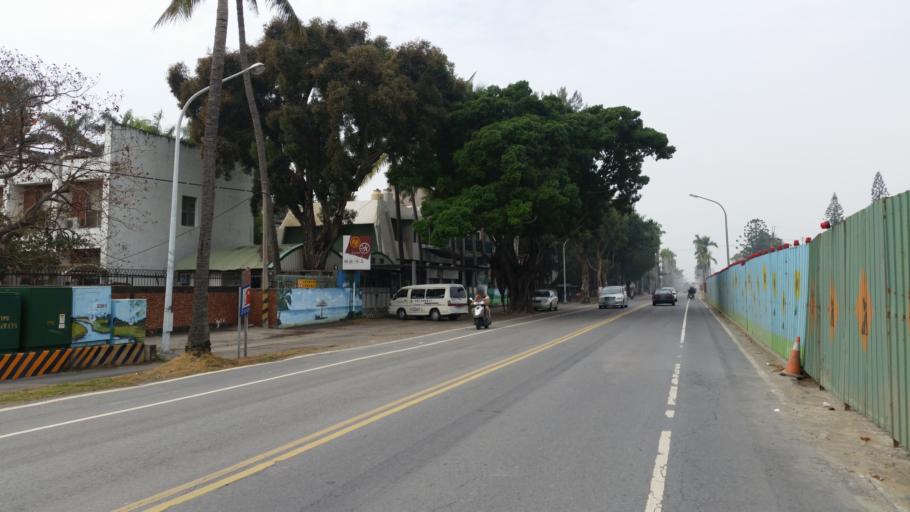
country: TW
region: Taiwan
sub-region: Tainan
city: Tainan
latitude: 22.9649
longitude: 120.2233
